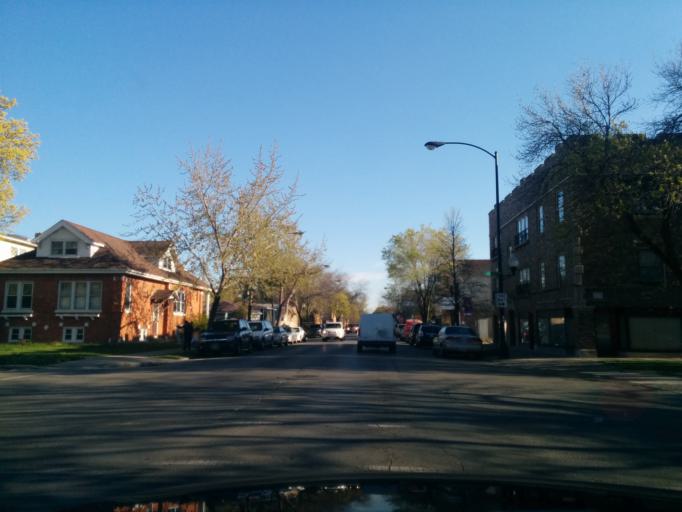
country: US
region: Illinois
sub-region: Cook County
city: Elmwood Park
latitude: 41.9380
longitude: -87.7567
